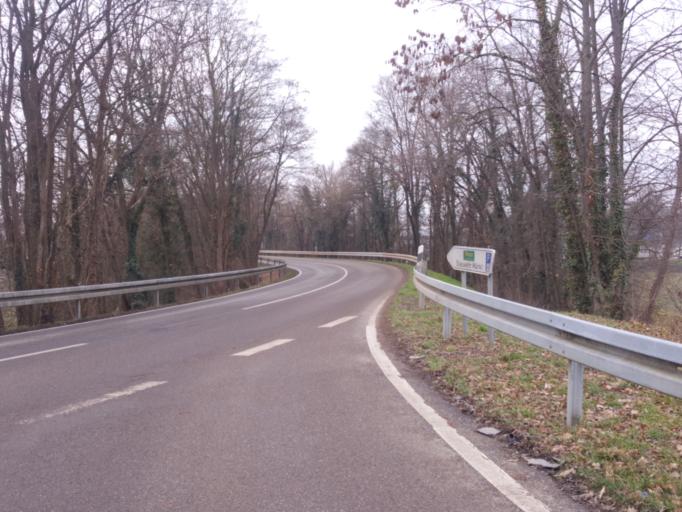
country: FR
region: Alsace
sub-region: Departement du Haut-Rhin
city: Huningue
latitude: 47.6120
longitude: 7.5956
